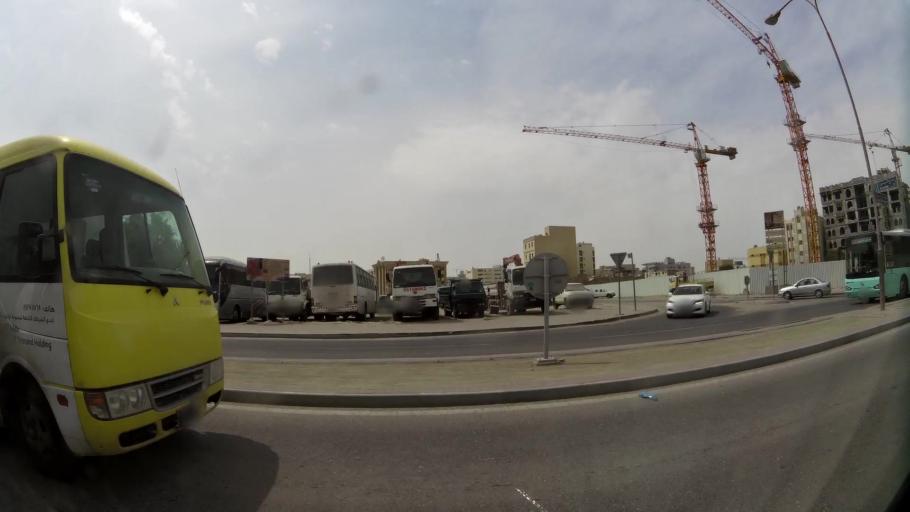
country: QA
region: Baladiyat ad Dawhah
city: Doha
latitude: 25.2838
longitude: 51.5402
